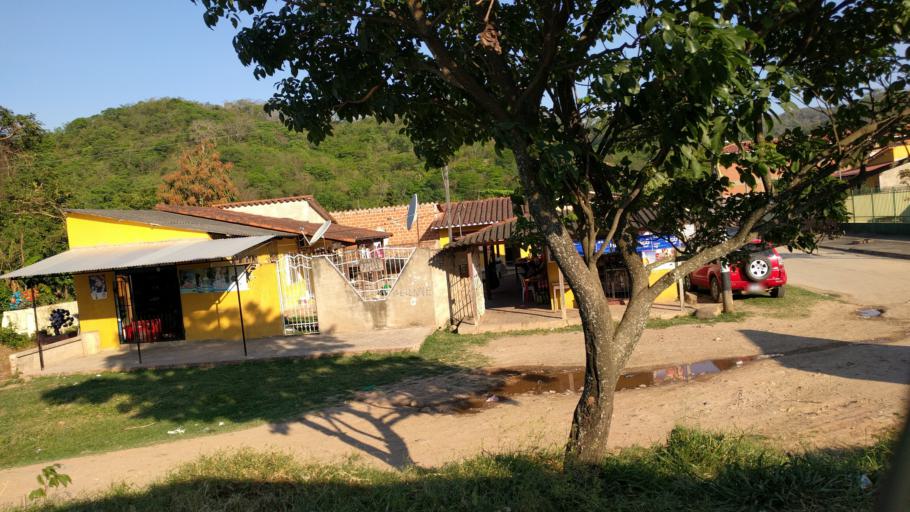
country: BO
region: Santa Cruz
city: Jorochito
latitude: -18.0594
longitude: -63.4309
